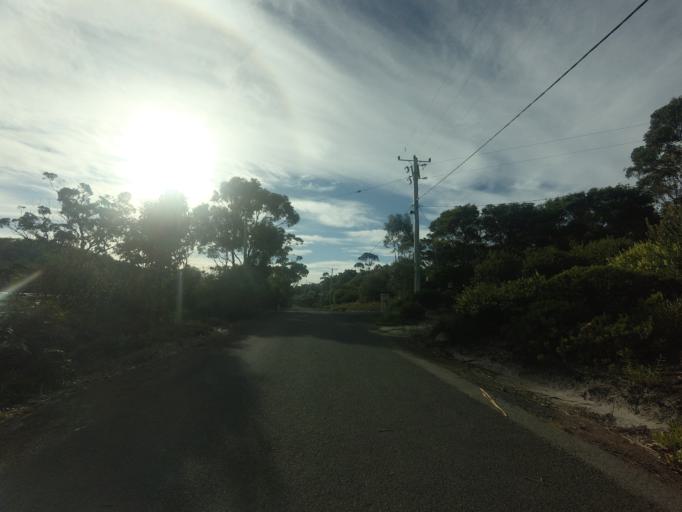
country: AU
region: Tasmania
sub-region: Sorell
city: Sorell
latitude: -42.9727
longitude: 147.8355
